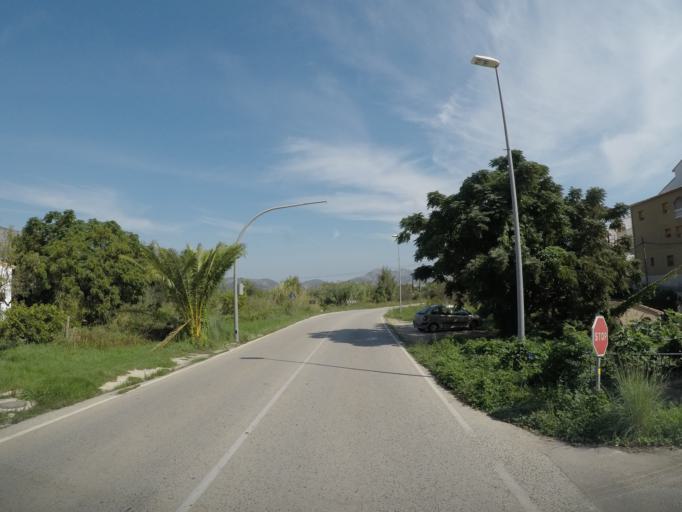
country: ES
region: Valencia
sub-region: Provincia de Alicante
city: Orba
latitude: 38.7806
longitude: -0.0656
